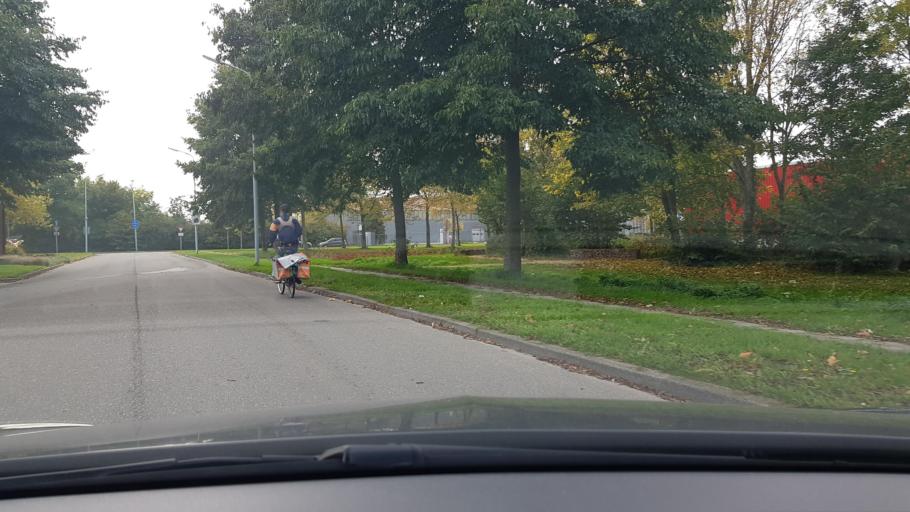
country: NL
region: South Holland
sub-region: Gemeente Kaag en Braassem
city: Leimuiden
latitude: 52.2660
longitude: 4.6453
